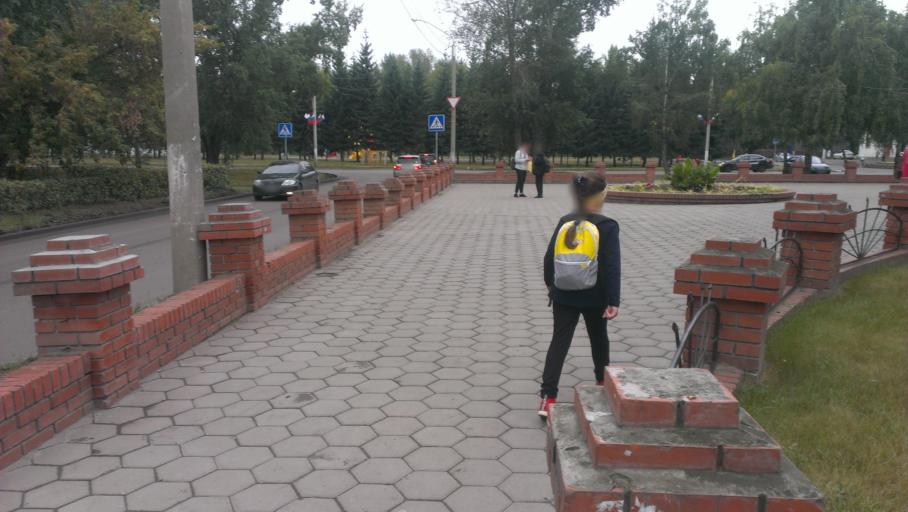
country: RU
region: Altai Krai
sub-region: Gorod Barnaulskiy
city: Barnaul
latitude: 53.3662
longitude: 83.6890
